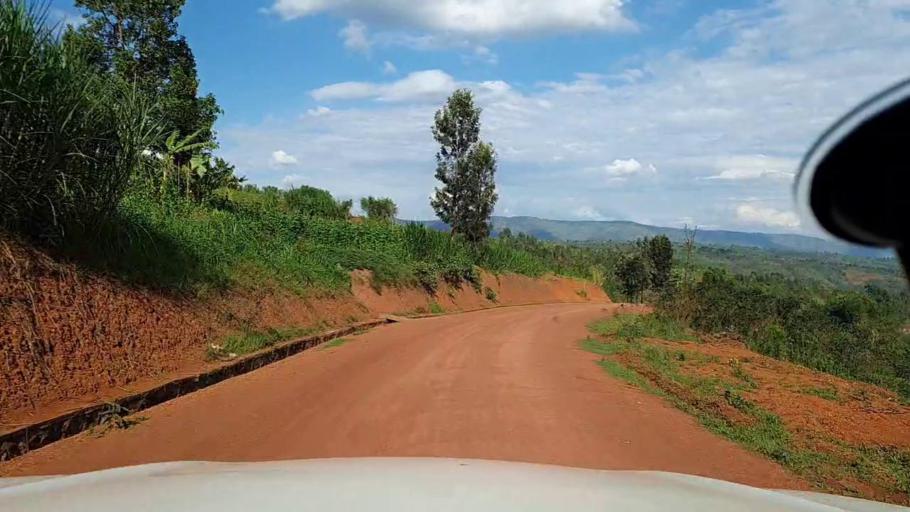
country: RW
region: Kigali
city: Kigali
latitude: -1.8399
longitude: 29.8513
